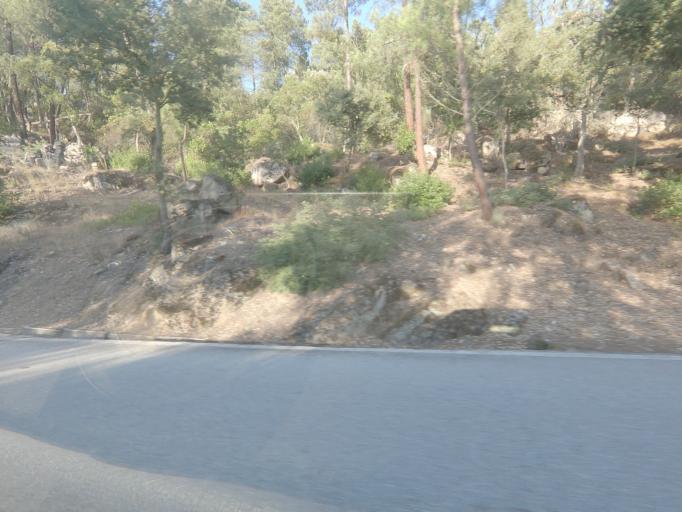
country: PT
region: Viseu
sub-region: Armamar
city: Armamar
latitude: 41.1148
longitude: -7.6737
